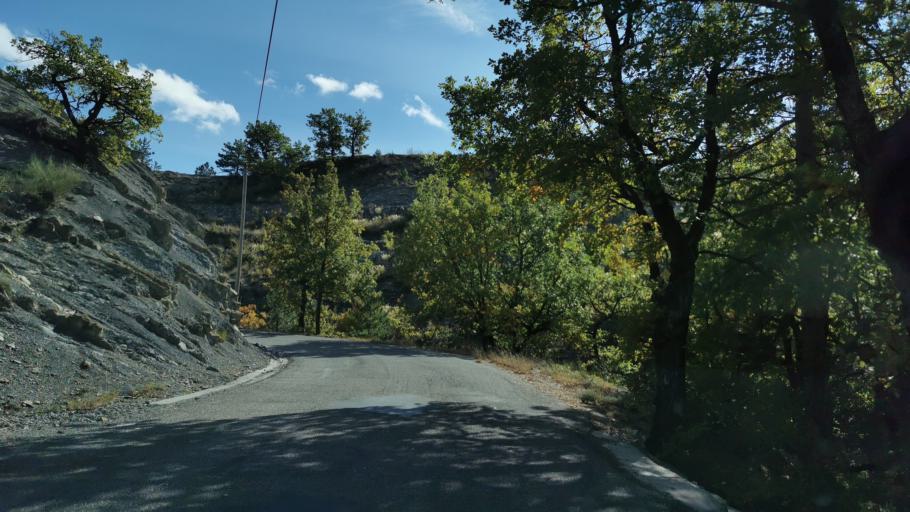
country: FR
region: Provence-Alpes-Cote d'Azur
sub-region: Departement des Alpes-de-Haute-Provence
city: Sisteron
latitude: 44.1869
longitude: 6.0123
